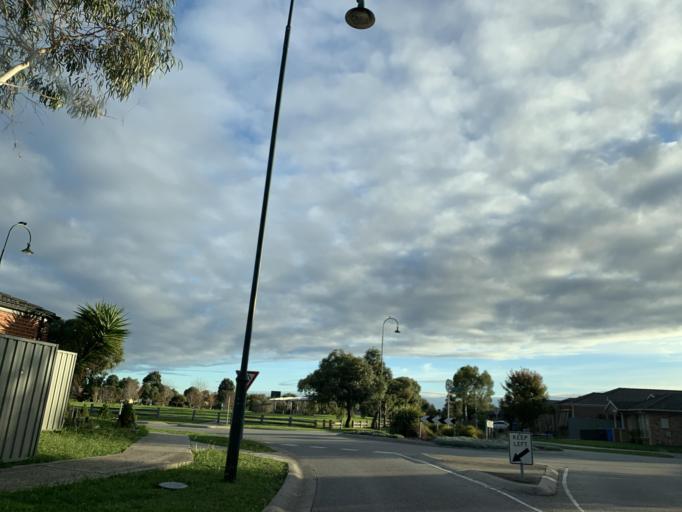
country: AU
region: Victoria
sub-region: Casey
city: Cranbourne East
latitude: -38.1127
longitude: 145.3058
